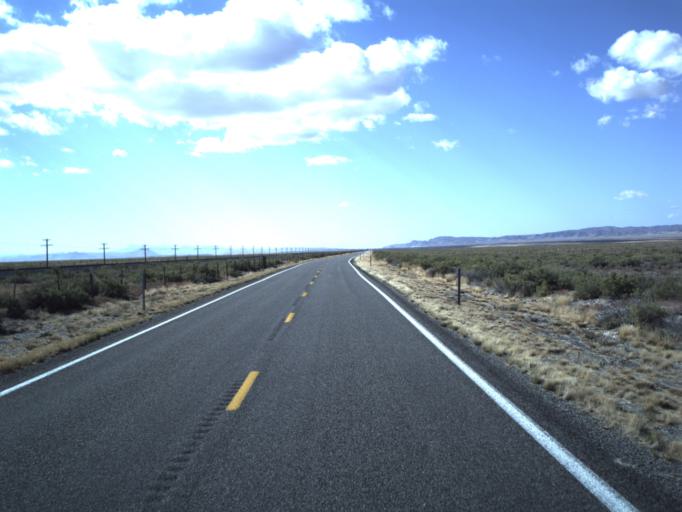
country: US
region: Utah
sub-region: Millard County
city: Delta
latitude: 39.1039
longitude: -112.7462
